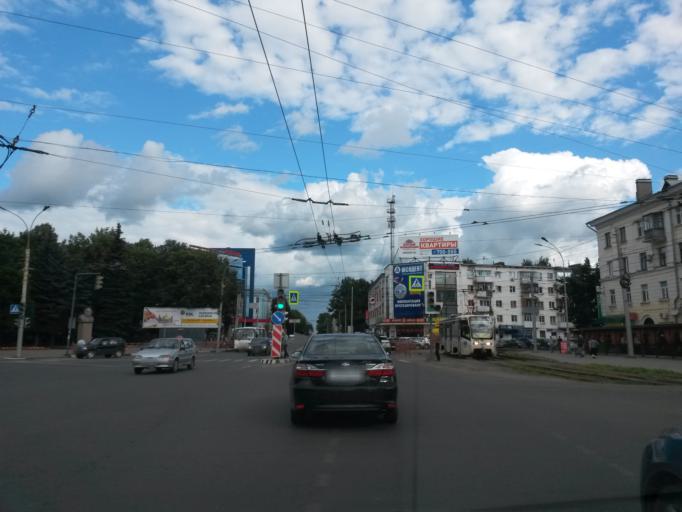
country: RU
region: Jaroslavl
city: Yaroslavl
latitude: 57.6360
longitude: 39.8651
